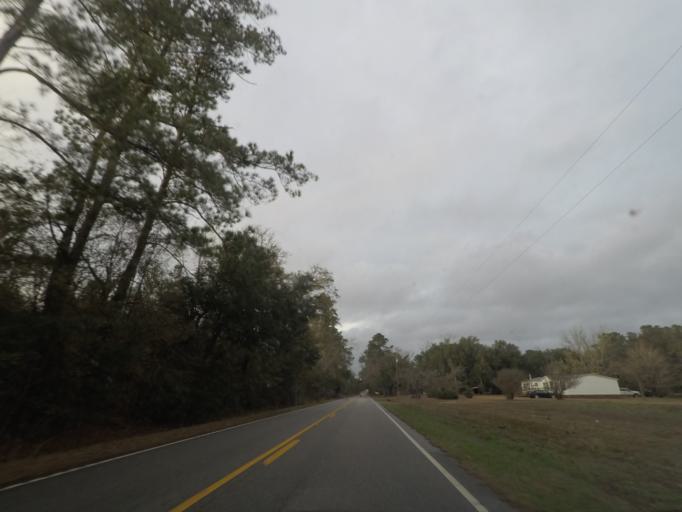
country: US
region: South Carolina
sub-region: Colleton County
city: Walterboro
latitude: 33.0346
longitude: -80.5916
